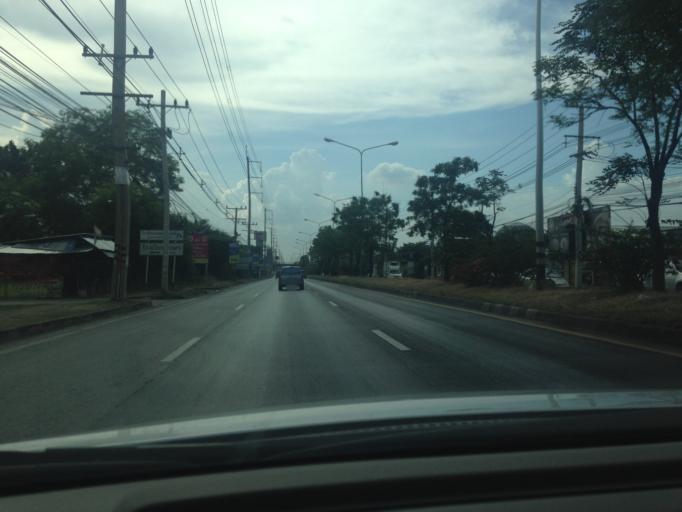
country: TH
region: Pathum Thani
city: Khlong Luang
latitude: 14.0660
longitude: 100.6667
